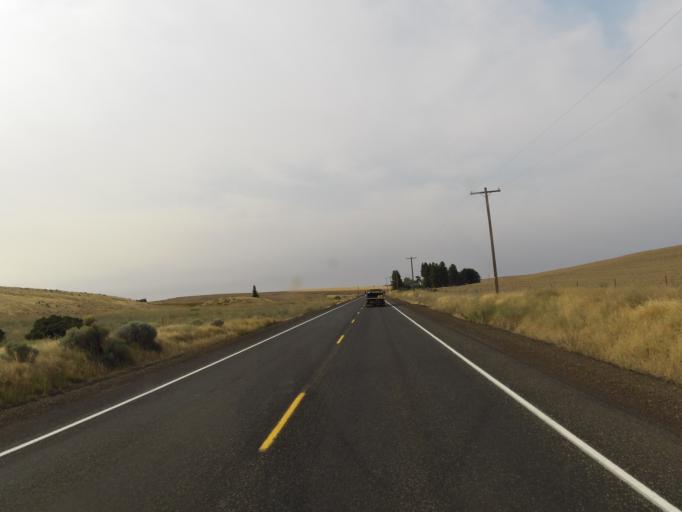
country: US
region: Oregon
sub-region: Sherman County
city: Moro
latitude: 45.4500
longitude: -120.7526
